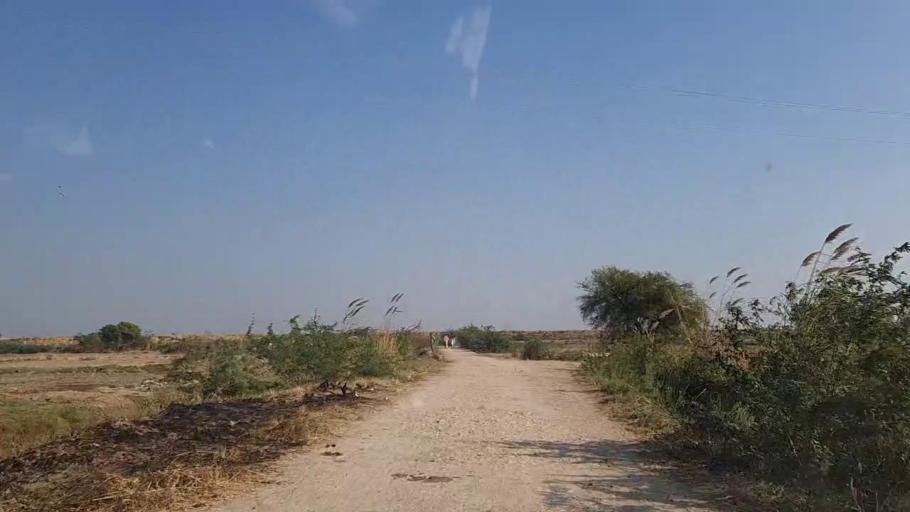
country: PK
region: Sindh
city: Thatta
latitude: 24.7392
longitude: 67.9682
